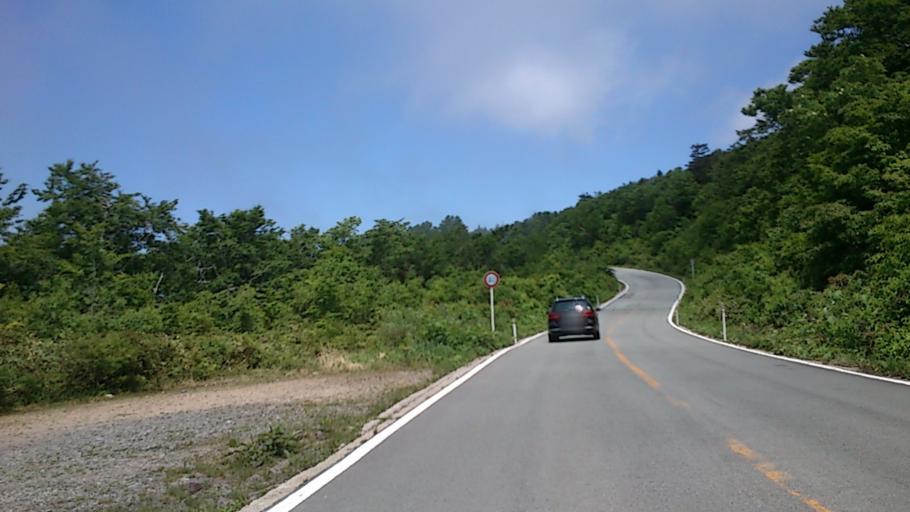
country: JP
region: Yamagata
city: Yamagata-shi
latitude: 38.1198
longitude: 140.4234
